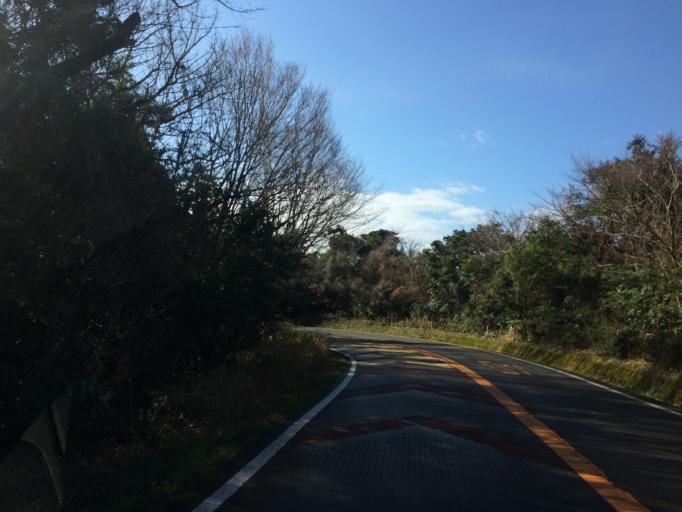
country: JP
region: Shizuoka
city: Shizuoka-shi
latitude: 34.9657
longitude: 138.4478
